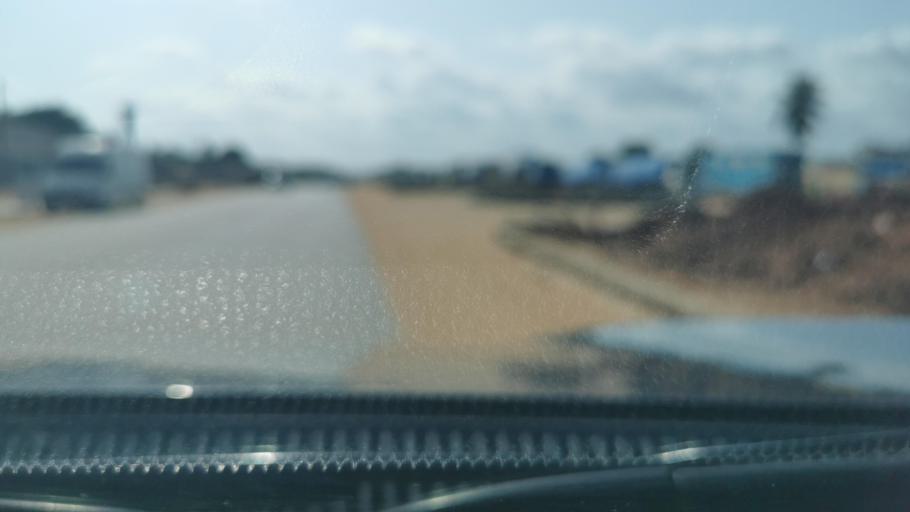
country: TG
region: Maritime
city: Lome
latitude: 6.2111
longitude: 1.1362
